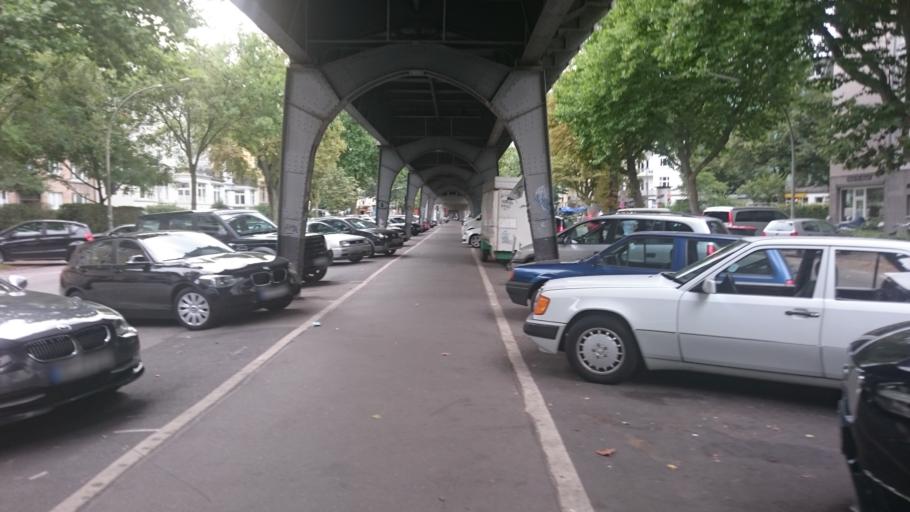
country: DE
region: Hamburg
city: Hamburg-Nord
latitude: 53.5808
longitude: 9.9810
